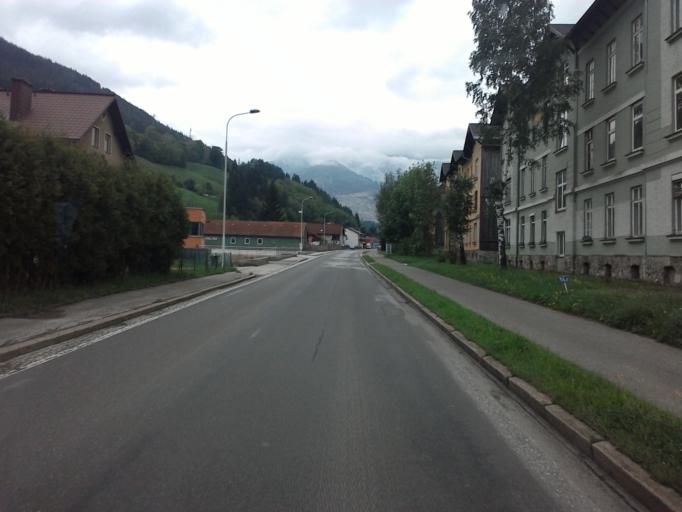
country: AT
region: Styria
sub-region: Politischer Bezirk Leoben
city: Eisenerz
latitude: 47.5580
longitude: 14.8685
